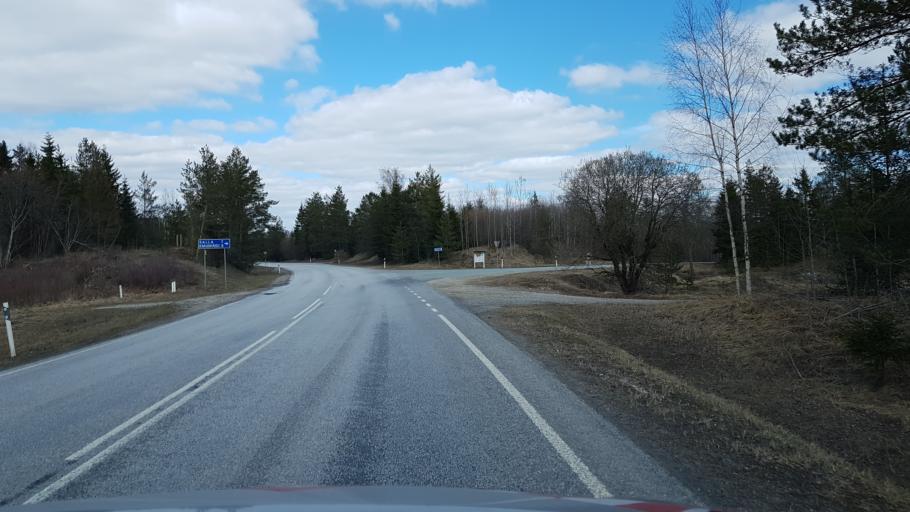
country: EE
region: Laeaene-Virumaa
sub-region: Rakke vald
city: Rakke
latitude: 58.9355
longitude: 26.2783
